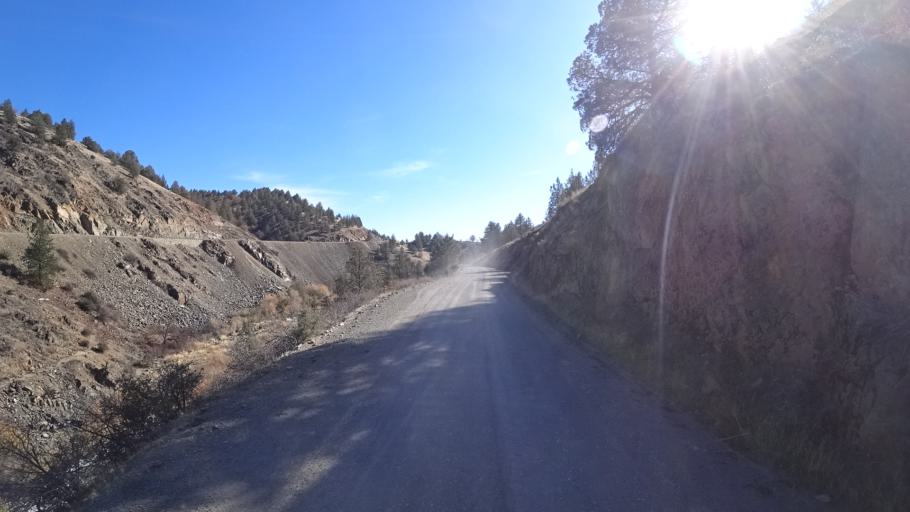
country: US
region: California
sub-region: Siskiyou County
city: Yreka
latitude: 41.7879
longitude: -122.6041
